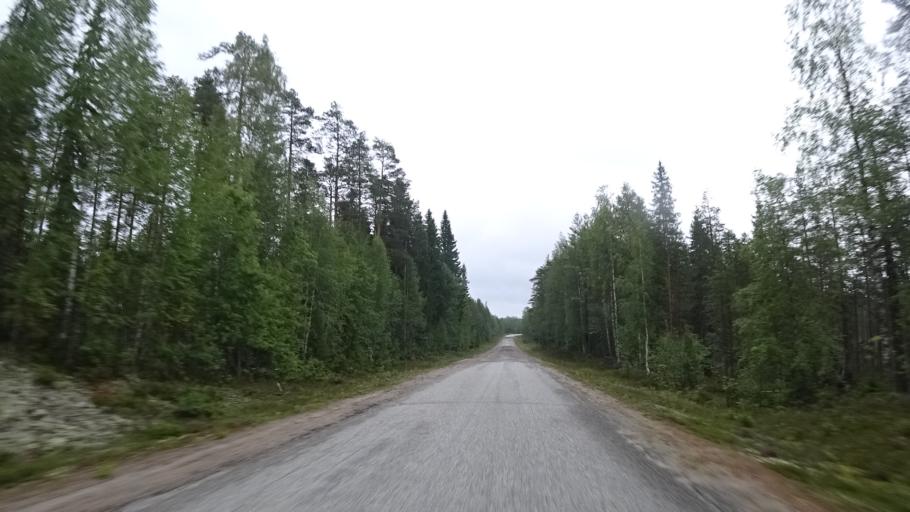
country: FI
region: North Karelia
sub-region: Joensuu
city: Ilomantsi
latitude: 63.2284
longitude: 30.8779
